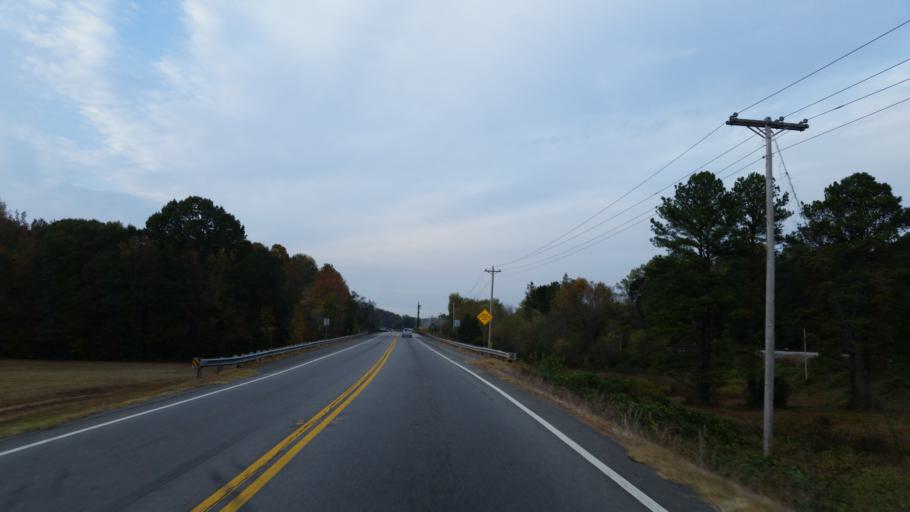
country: US
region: Georgia
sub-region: Gordon County
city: Calhoun
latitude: 34.5742
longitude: -84.9400
